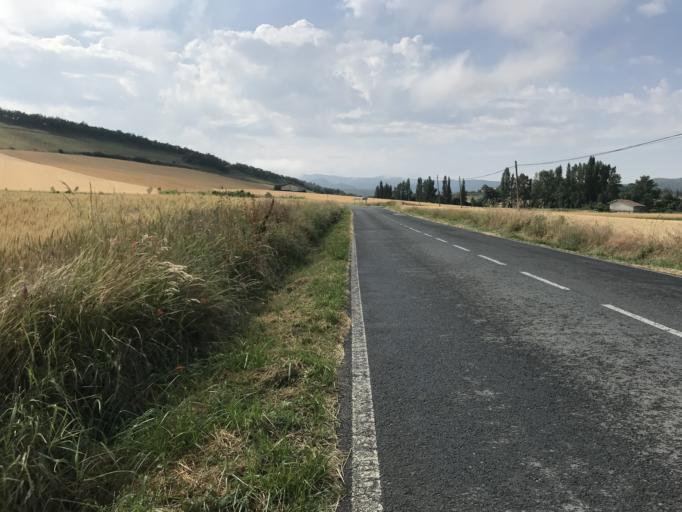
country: ES
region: Basque Country
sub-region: Provincia de Alava
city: Gasteiz / Vitoria
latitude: 42.8247
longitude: -2.6498
